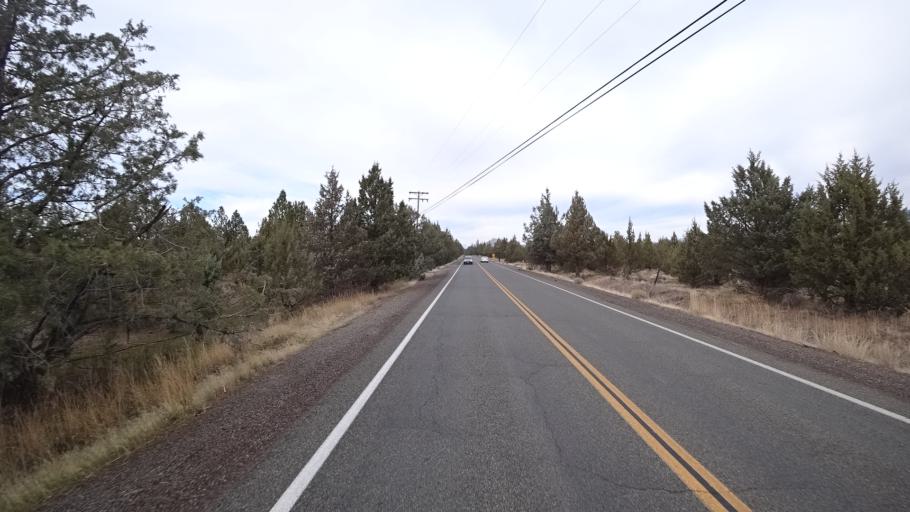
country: US
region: California
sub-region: Siskiyou County
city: Weed
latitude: 41.6114
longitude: -122.3671
